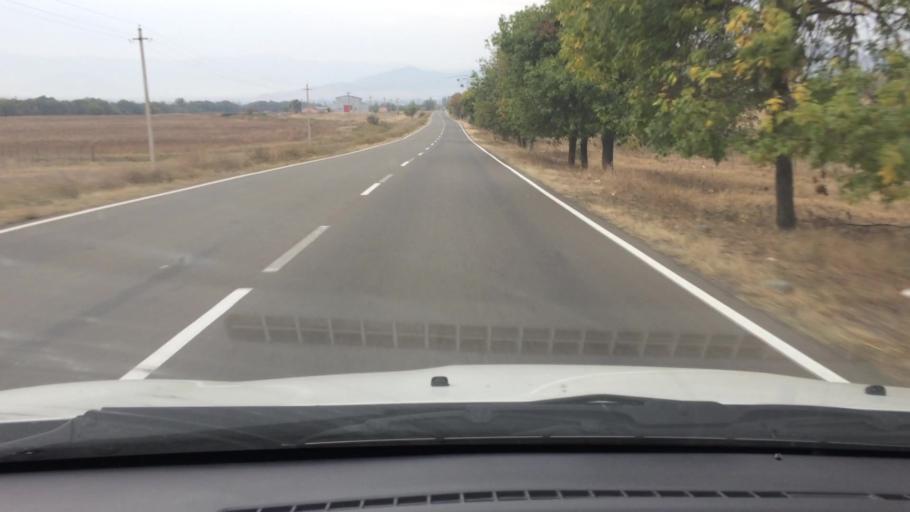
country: GE
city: Naghvarevi
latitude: 41.3432
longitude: 44.8138
